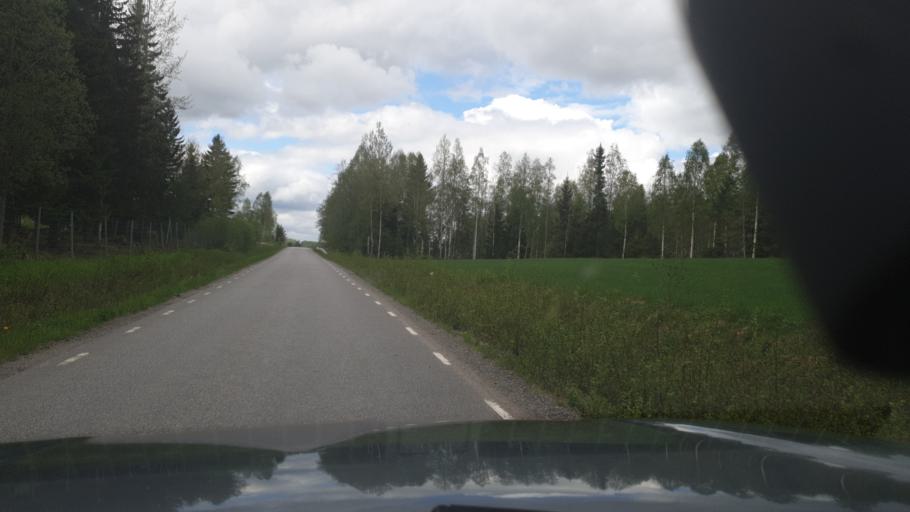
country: SE
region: Gaevleborg
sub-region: Ljusdals Kommun
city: Jaervsoe
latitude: 61.7305
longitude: 16.2847
